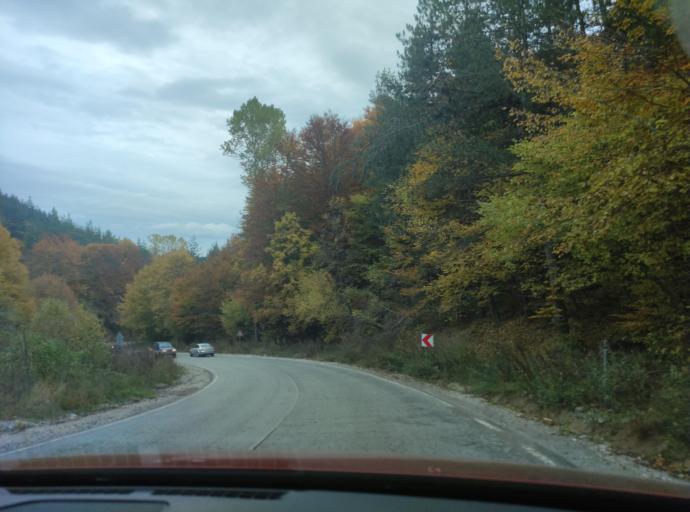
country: BG
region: Sofiya
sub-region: Obshtina Godech
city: Godech
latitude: 43.0202
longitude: 23.1352
